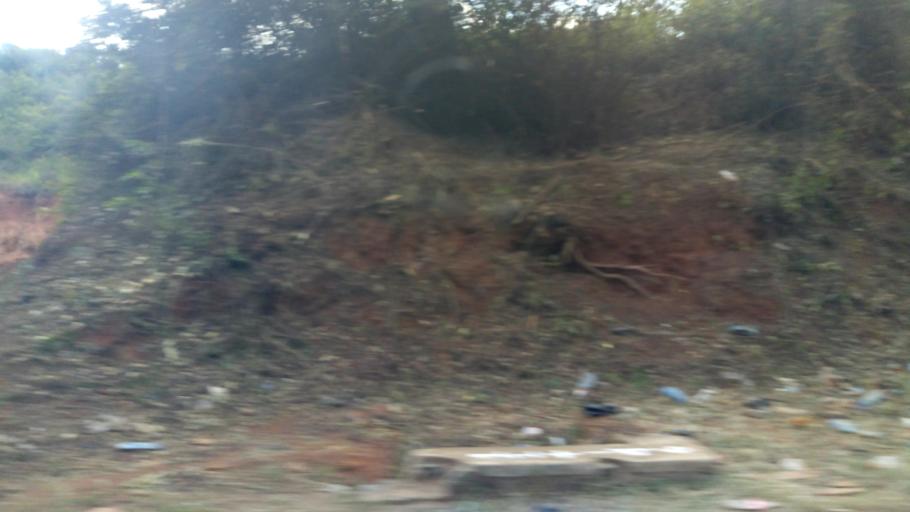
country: KE
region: Kiambu
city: Limuru
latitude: -1.0686
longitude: 36.6014
